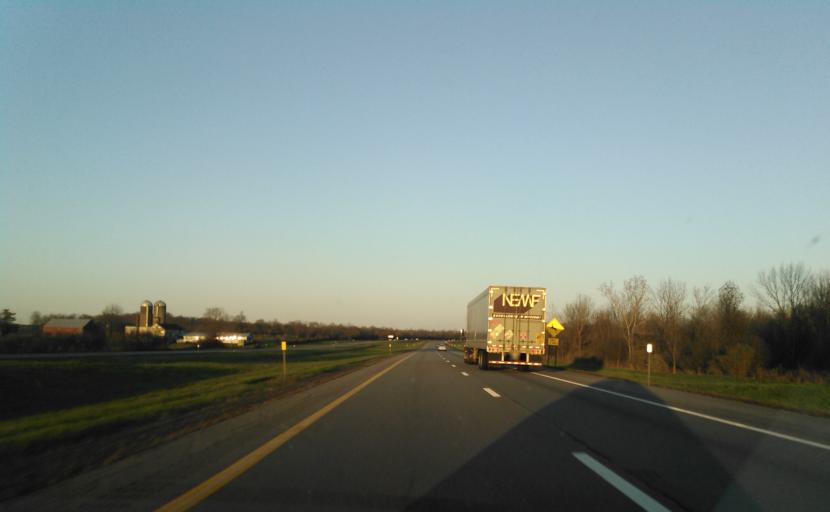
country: US
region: New York
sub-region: Ontario County
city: Clifton Springs
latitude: 42.9741
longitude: -77.1012
